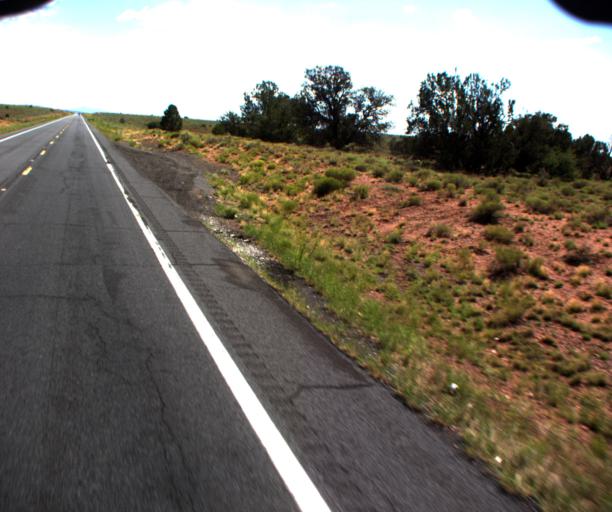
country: US
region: Arizona
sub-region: Coconino County
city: Williams
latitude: 35.6372
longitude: -112.1415
